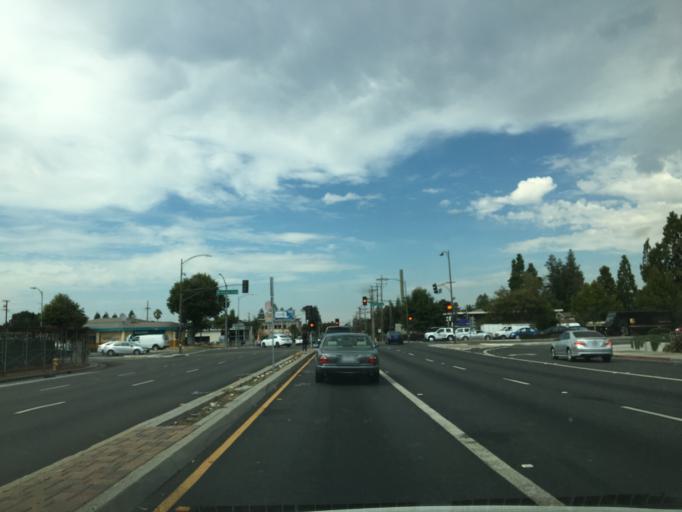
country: US
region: California
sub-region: Santa Clara County
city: Burbank
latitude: 37.3227
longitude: -121.9319
